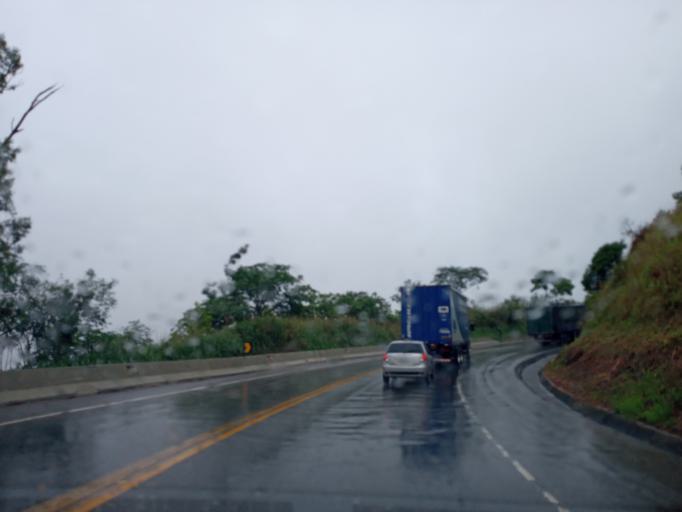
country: BR
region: Minas Gerais
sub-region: Luz
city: Luz
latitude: -19.7193
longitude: -45.8810
